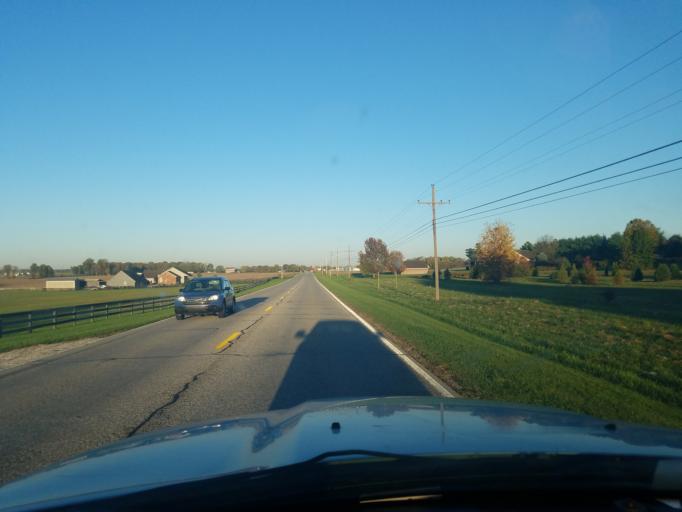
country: US
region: Indiana
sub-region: Floyd County
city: Galena
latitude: 38.3902
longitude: -86.0489
